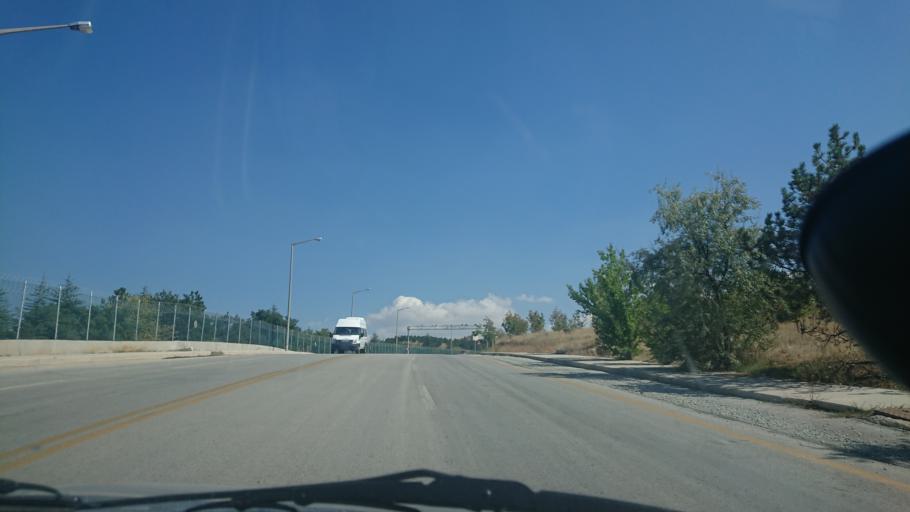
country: TR
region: Ankara
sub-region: Goelbasi
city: Golbasi
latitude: 39.8066
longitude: 32.8268
